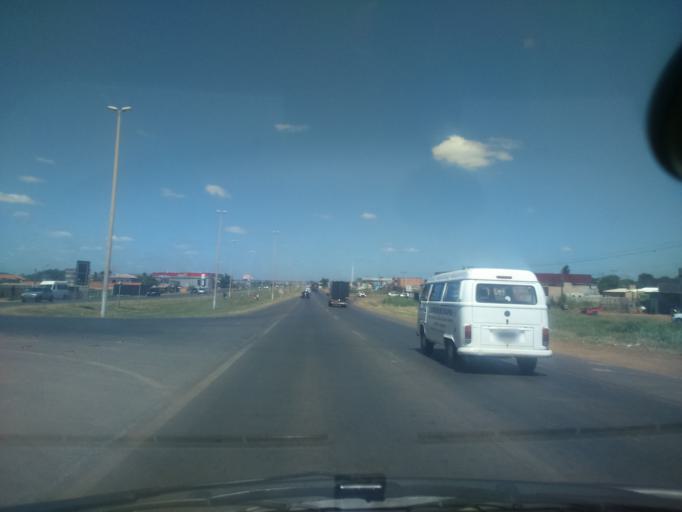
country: BR
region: Goias
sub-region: Luziania
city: Luziania
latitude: -16.1086
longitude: -47.9724
